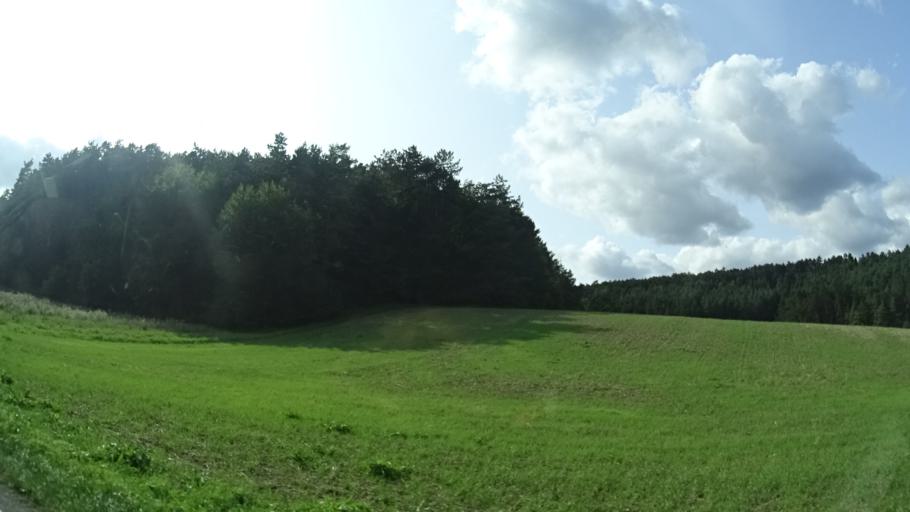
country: DE
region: Bavaria
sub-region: Regierungsbezirk Unterfranken
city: Greussenheim
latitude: 49.8422
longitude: 9.7942
